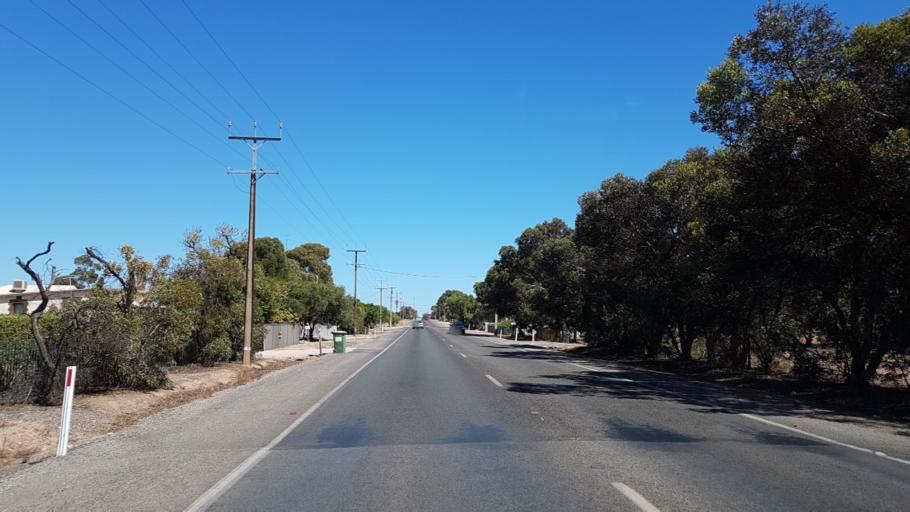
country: AU
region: South Australia
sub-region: Copper Coast
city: Kadina
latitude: -33.9554
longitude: 137.6876
